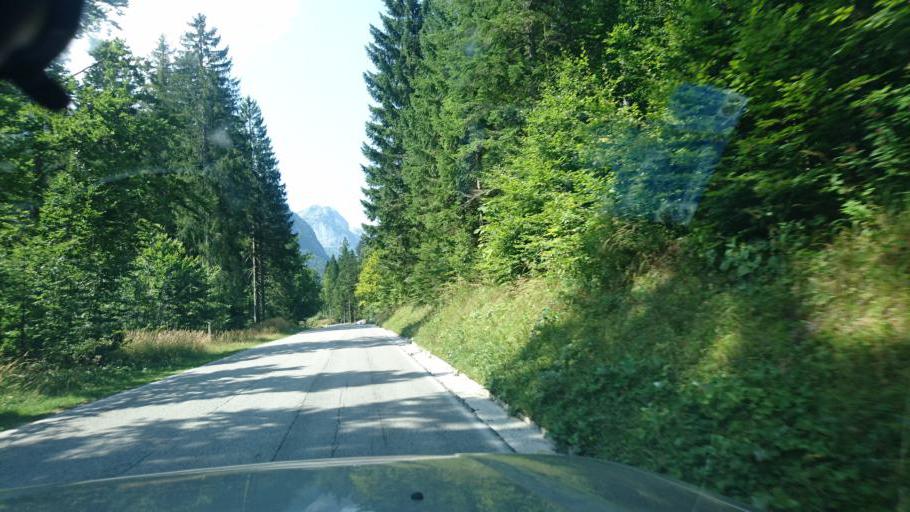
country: SI
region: Bovec
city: Bovec
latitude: 46.4010
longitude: 13.5114
